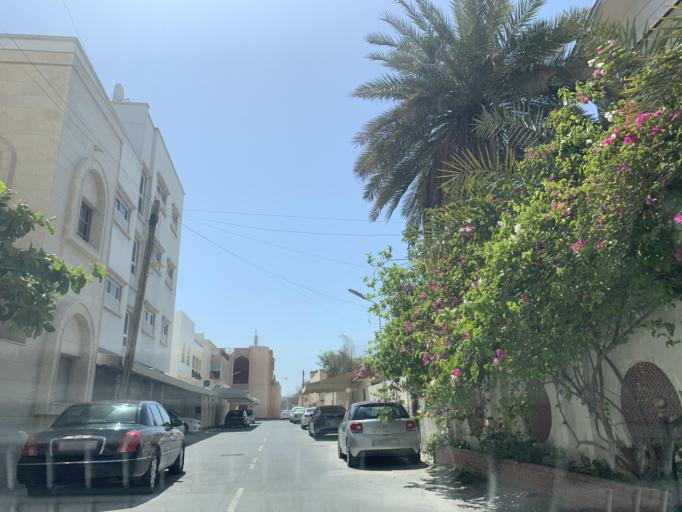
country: BH
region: Muharraq
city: Al Muharraq
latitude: 26.2656
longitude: 50.6183
